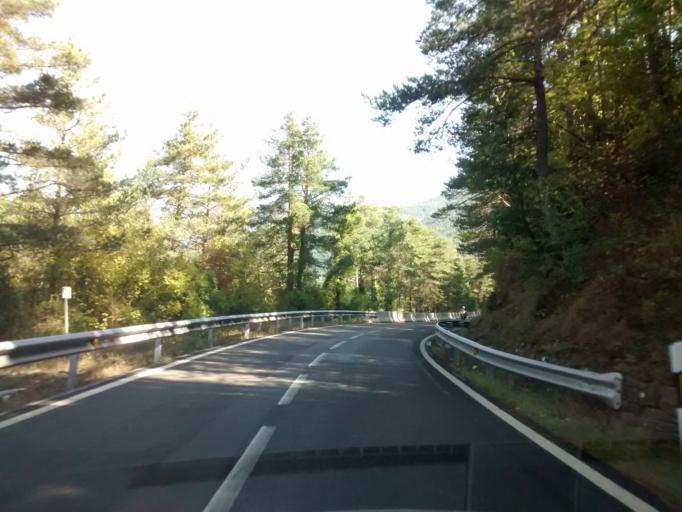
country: ES
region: Aragon
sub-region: Provincia de Huesca
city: Fiscal
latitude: 42.5414
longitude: -0.1342
